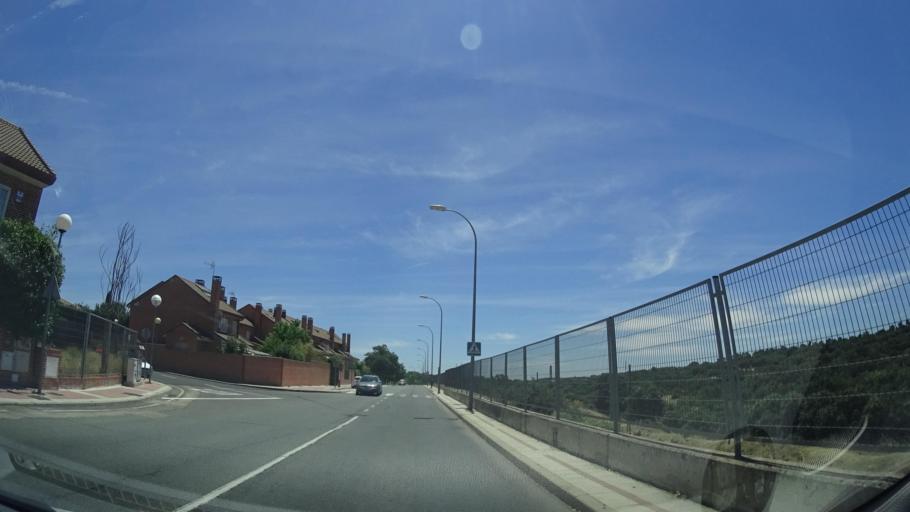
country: ES
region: Madrid
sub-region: Provincia de Madrid
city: Collado-Villalba
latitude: 40.6228
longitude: -3.9974
